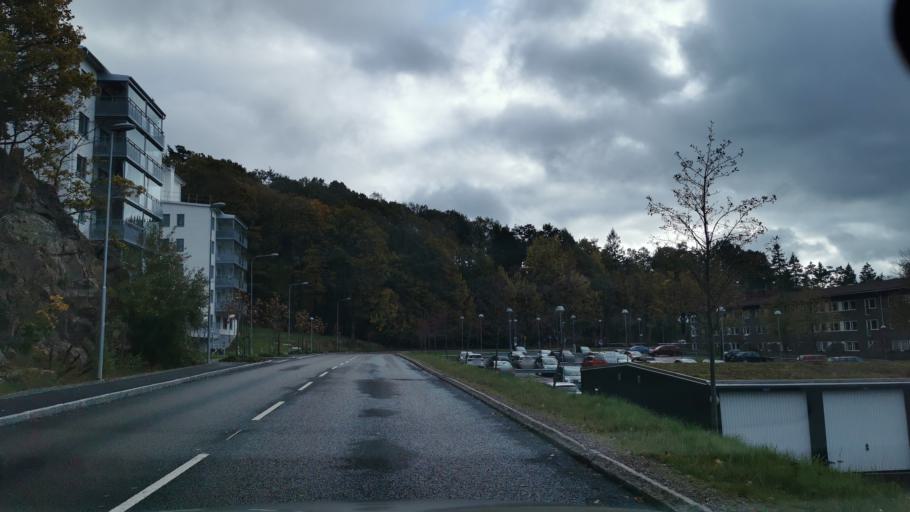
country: SE
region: Vaestra Goetaland
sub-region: Partille Kommun
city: Partille
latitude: 57.7203
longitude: 12.0822
